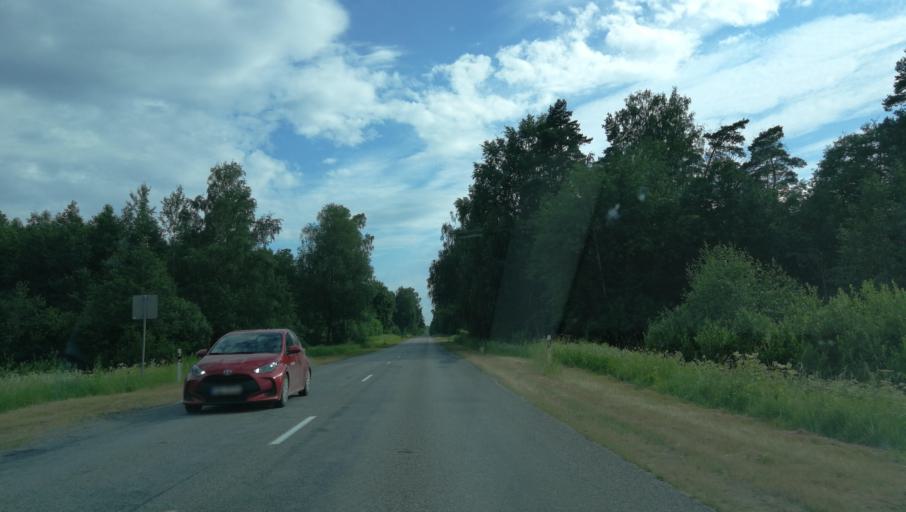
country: LV
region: Valmieras Rajons
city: Valmiera
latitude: 57.5844
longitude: 25.4589
